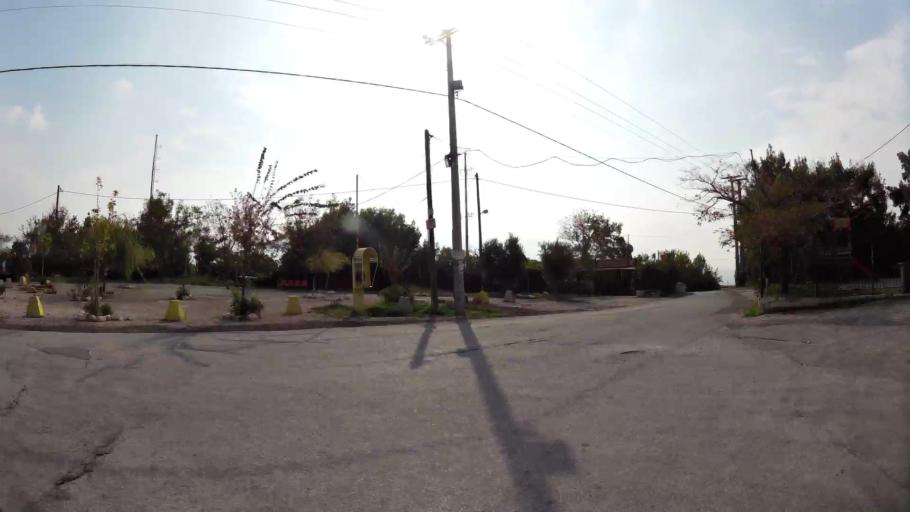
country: GR
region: Attica
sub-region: Nomarchia Athinas
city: Galatsi
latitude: 38.0037
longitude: 23.7551
